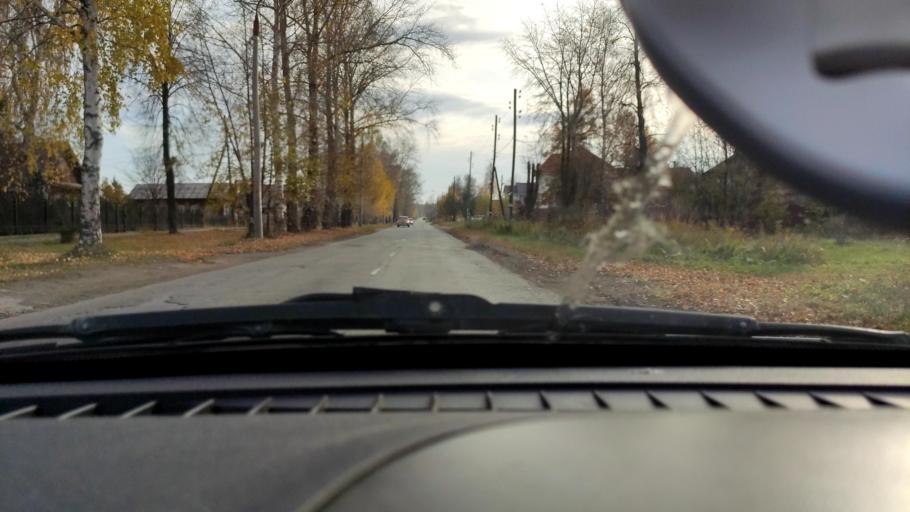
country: RU
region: Perm
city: Polazna
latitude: 58.1235
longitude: 56.4002
